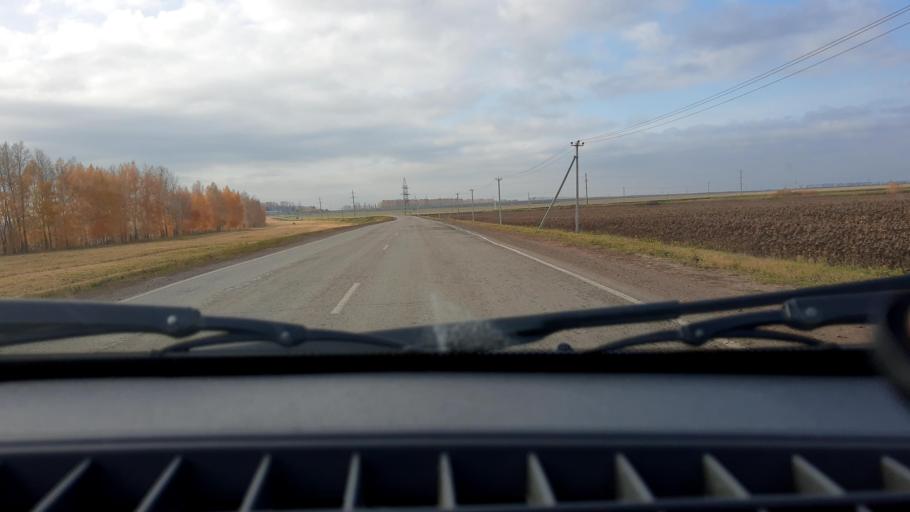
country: RU
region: Bashkortostan
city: Kabakovo
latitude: 54.5401
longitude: 56.0755
